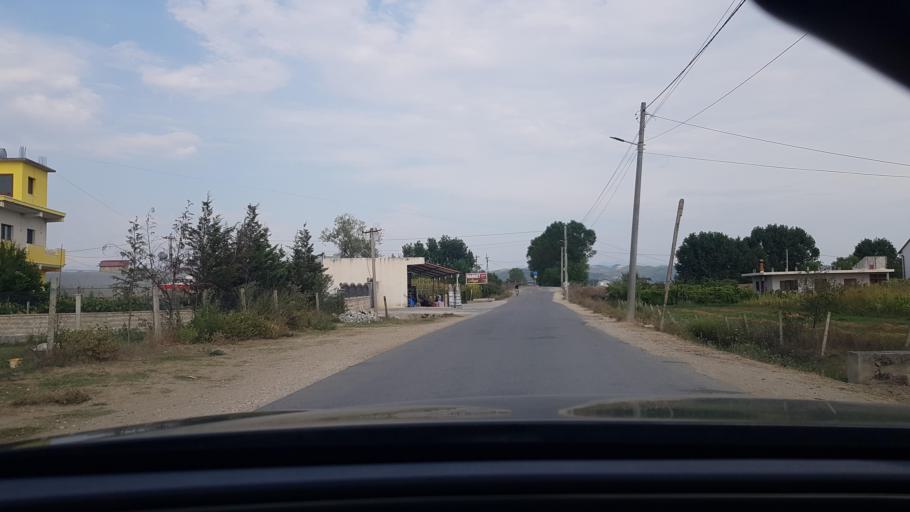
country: AL
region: Durres
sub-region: Rrethi i Durresit
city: Katundi i Ri
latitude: 41.4853
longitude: 19.5244
